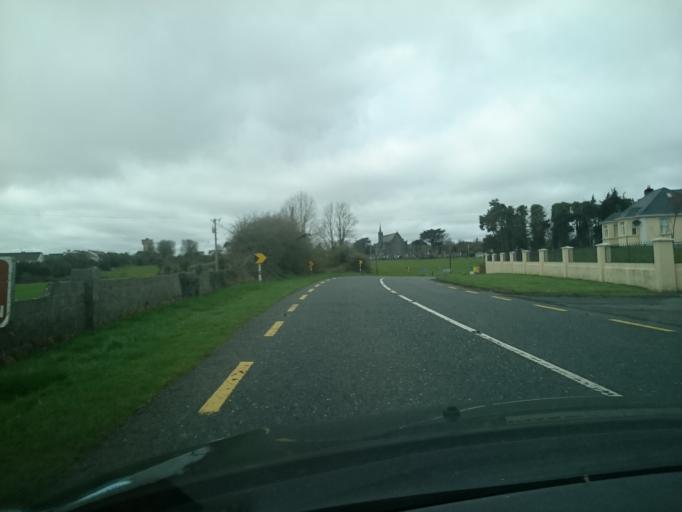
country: IE
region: Connaught
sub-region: Maigh Eo
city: Kiltamagh
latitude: 53.8008
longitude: -9.1231
